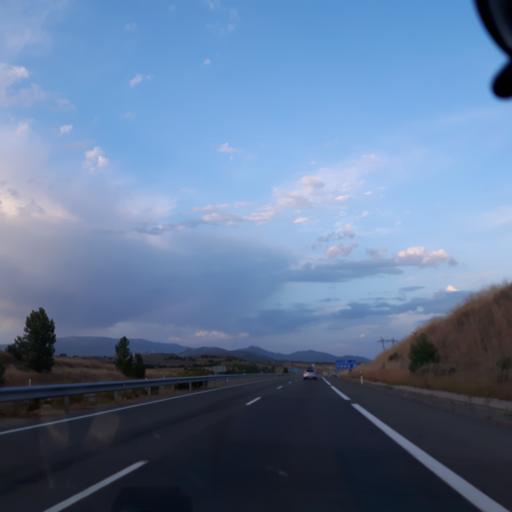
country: ES
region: Castille and Leon
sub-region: Provincia de Salamanca
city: Guijuelo
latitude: 40.5341
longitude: -5.6660
